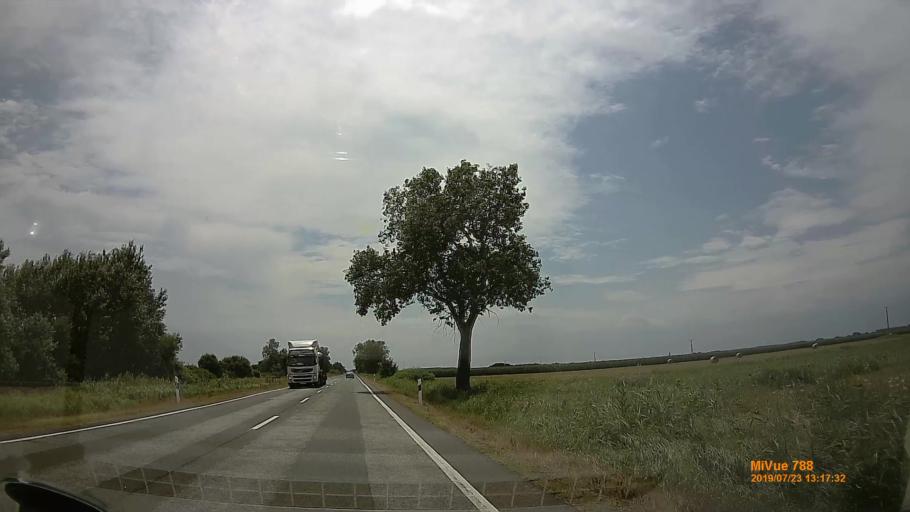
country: HU
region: Hajdu-Bihar
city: Polgar
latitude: 47.8977
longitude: 21.1563
